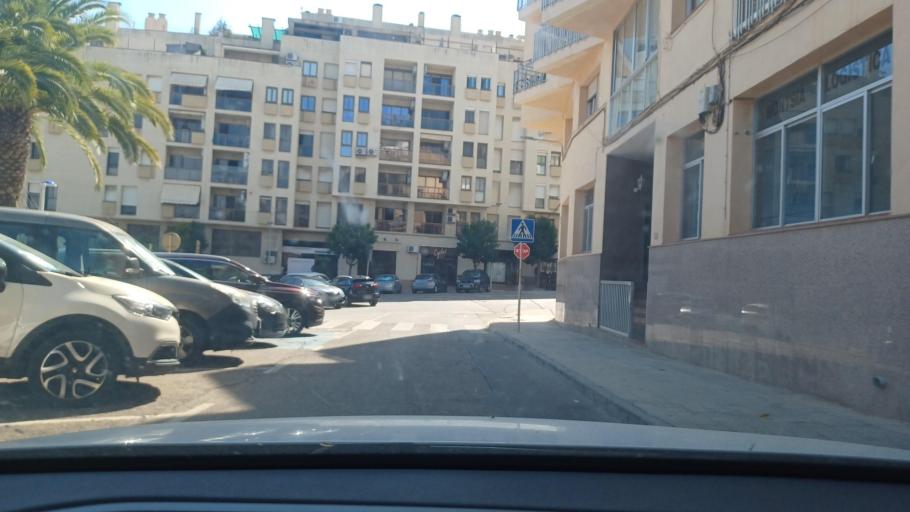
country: ES
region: Catalonia
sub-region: Provincia de Tarragona
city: Sant Carles de la Rapita
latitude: 40.6171
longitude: 0.5930
